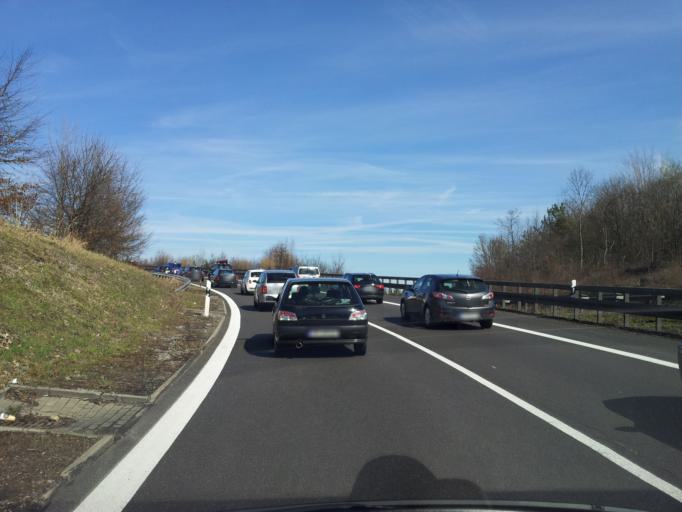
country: DE
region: Baden-Wuerttemberg
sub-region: Regierungsbezirk Stuttgart
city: Sindelfingen
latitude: 48.7260
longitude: 9.0709
